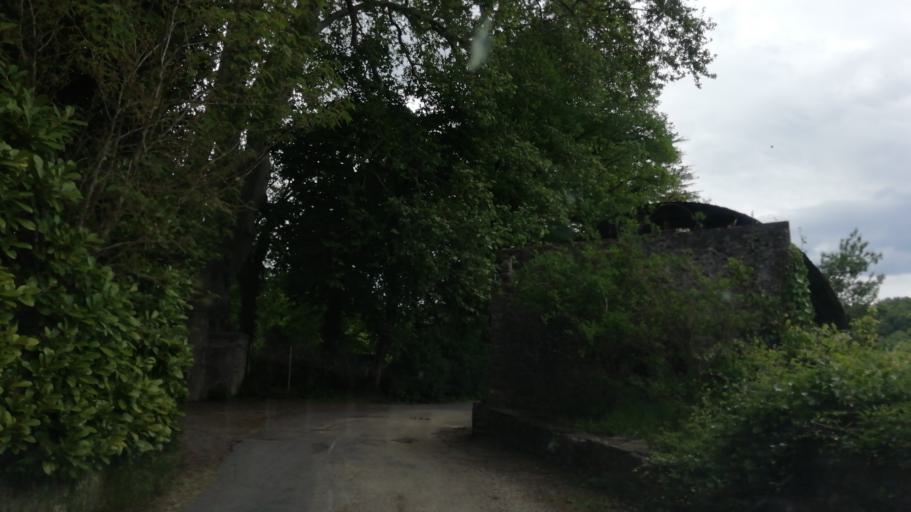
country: FR
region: Languedoc-Roussillon
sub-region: Departement de l'Herault
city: Cazilhac
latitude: 43.9230
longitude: 3.7118
